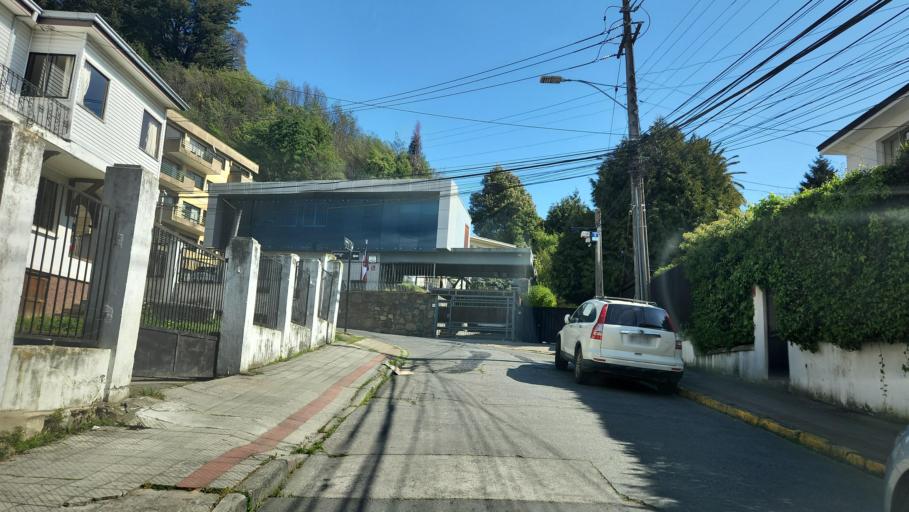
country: CL
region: Biobio
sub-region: Provincia de Concepcion
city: Concepcion
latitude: -36.8302
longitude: -73.0410
